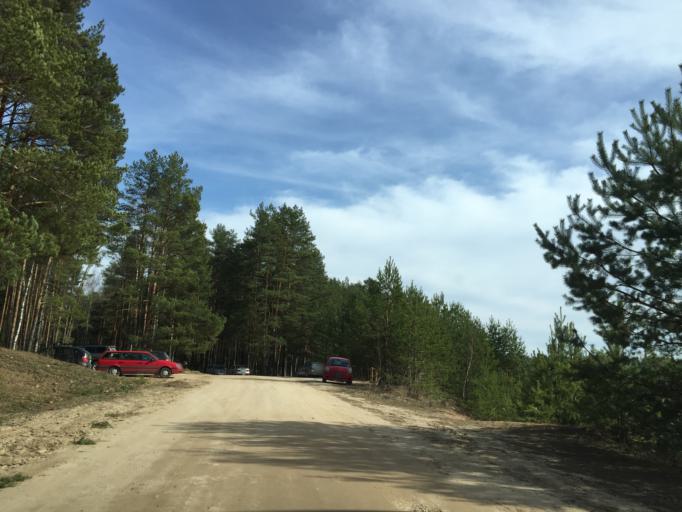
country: LV
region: Ikskile
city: Ikskile
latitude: 56.8412
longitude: 24.5524
